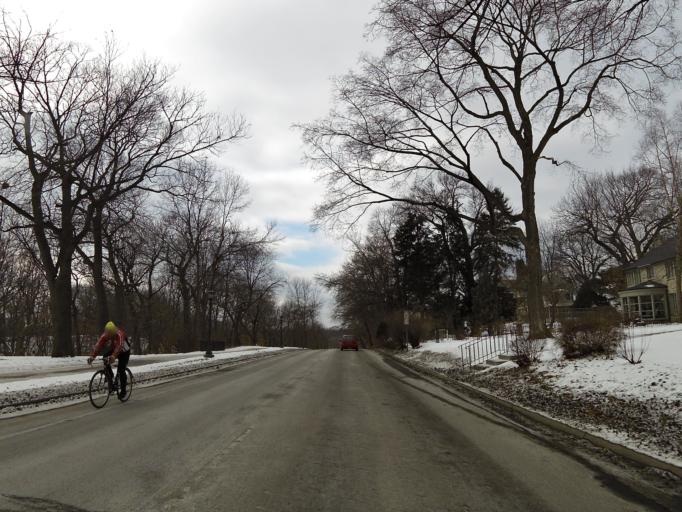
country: US
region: Minnesota
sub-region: Ramsey County
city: Falcon Heights
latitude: 44.9432
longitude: -93.1950
